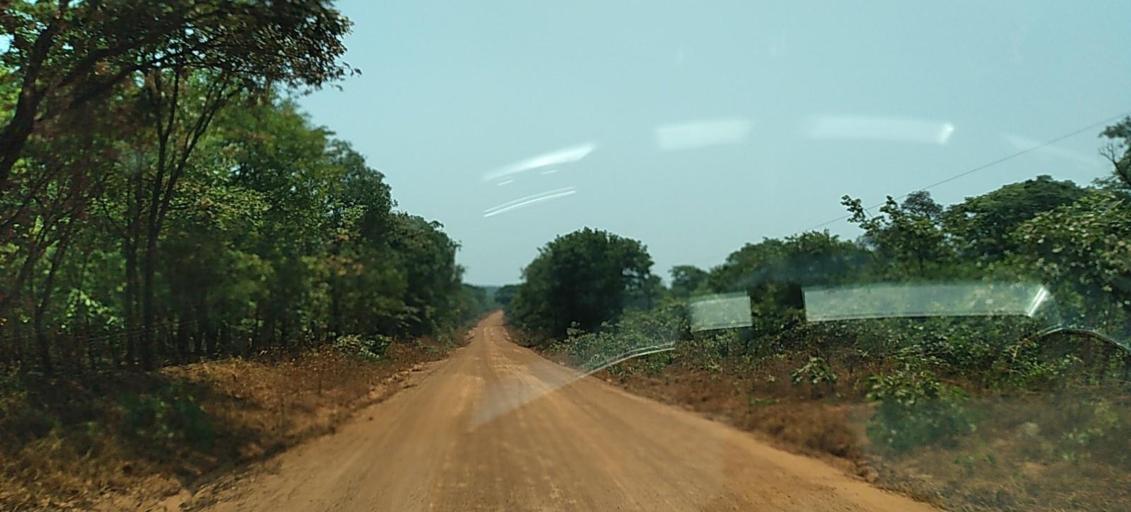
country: ZM
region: North-Western
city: Kansanshi
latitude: -11.9893
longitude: 26.8422
